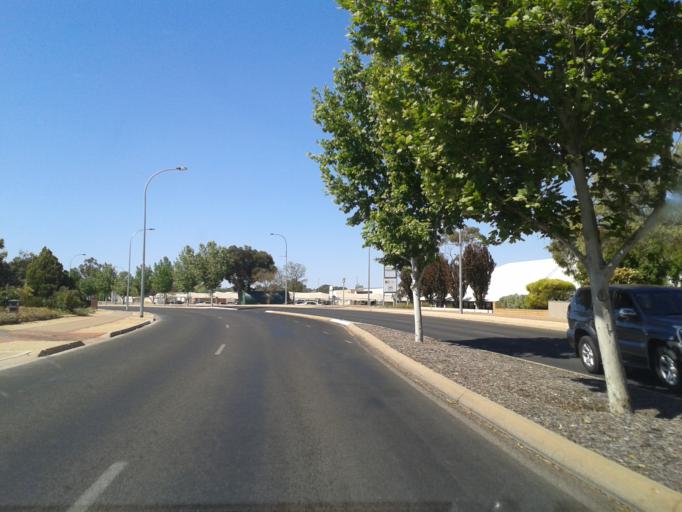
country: AU
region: South Australia
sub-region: Berri and Barmera
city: Berri
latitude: -34.2811
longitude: 140.6068
